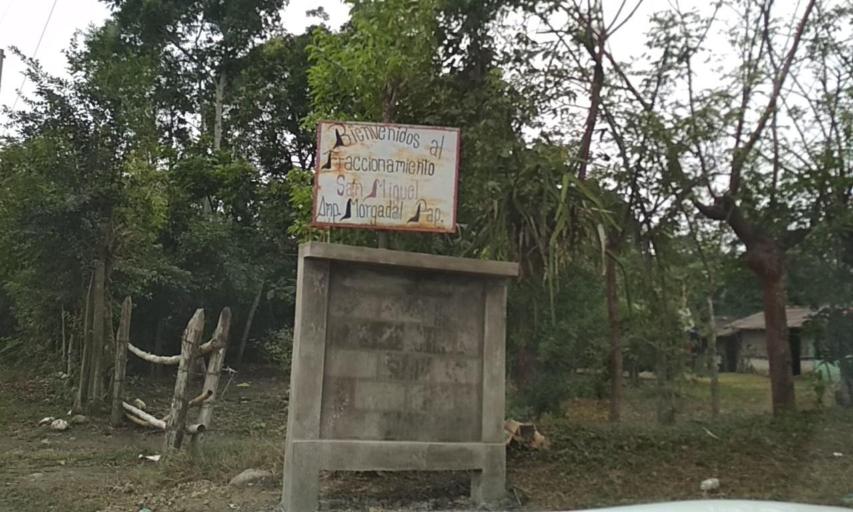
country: MX
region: Veracruz
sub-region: Papantla
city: El Chote
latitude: 20.3921
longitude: -97.3527
